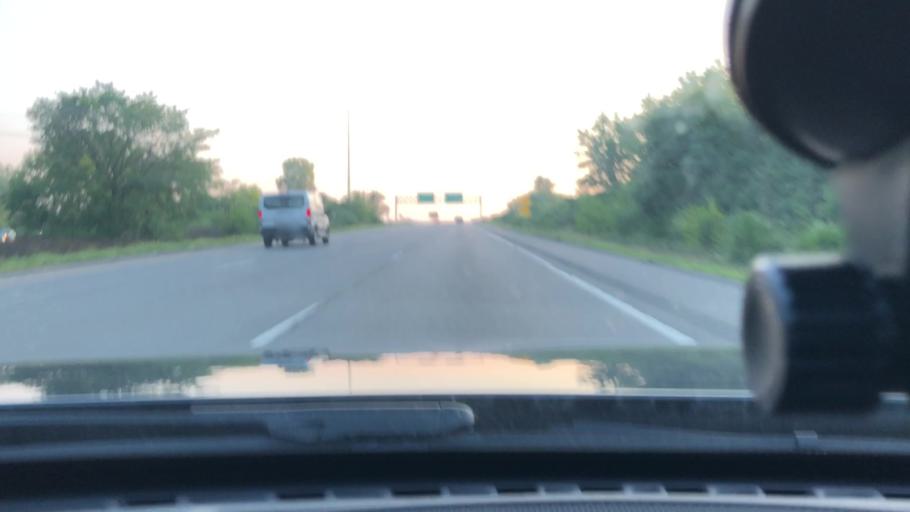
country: US
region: Michigan
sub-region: Washtenaw County
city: Ann Arbor
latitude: 42.3144
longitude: -83.7406
